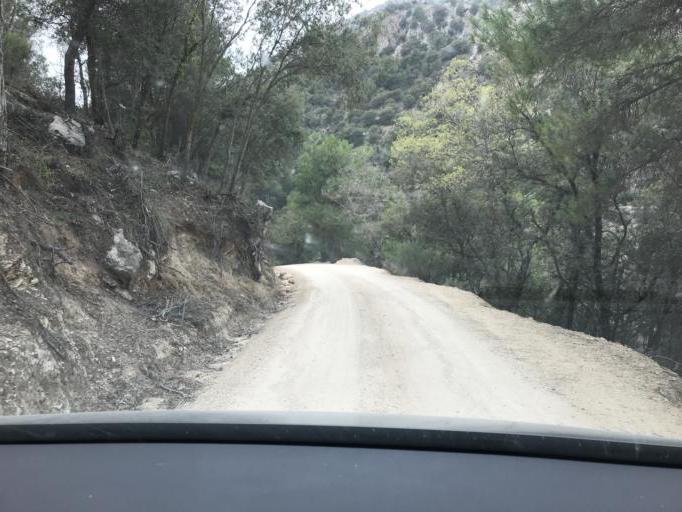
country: ES
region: Andalusia
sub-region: Provincia de Granada
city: Castril
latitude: 37.8799
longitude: -2.7550
